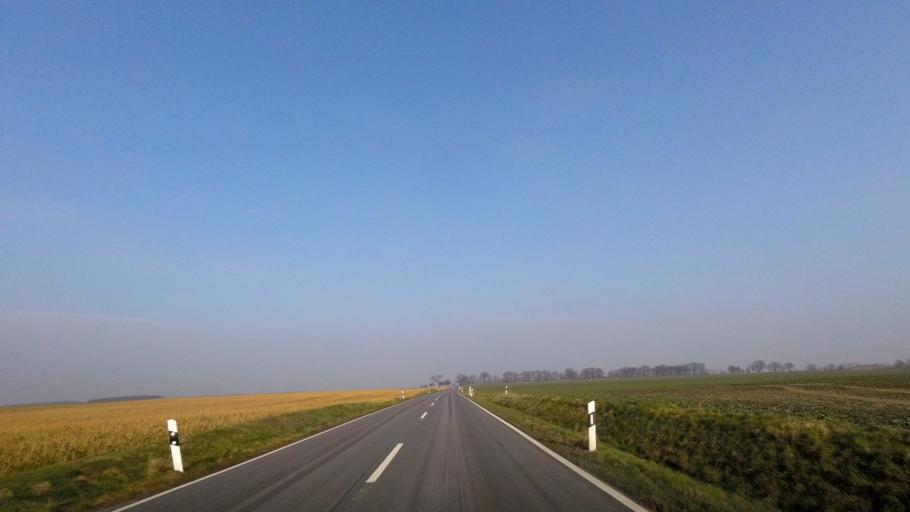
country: DE
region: Brandenburg
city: Niedergorsdorf
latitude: 51.9373
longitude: 13.0363
